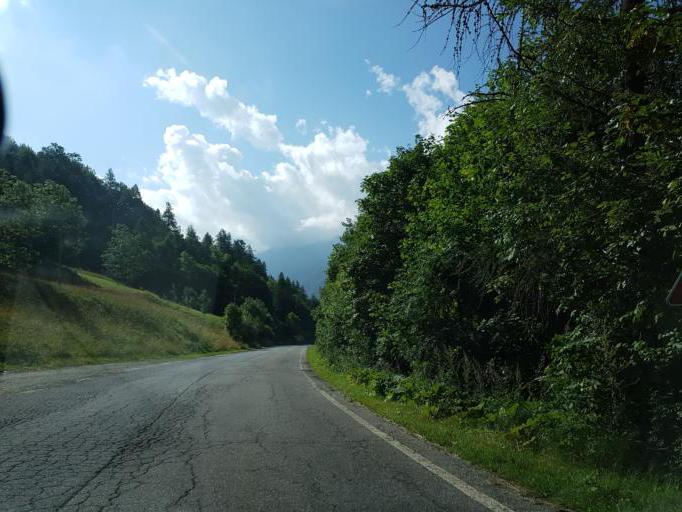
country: IT
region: Piedmont
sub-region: Provincia di Cuneo
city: Casteldelfino
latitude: 44.6067
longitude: 7.0613
